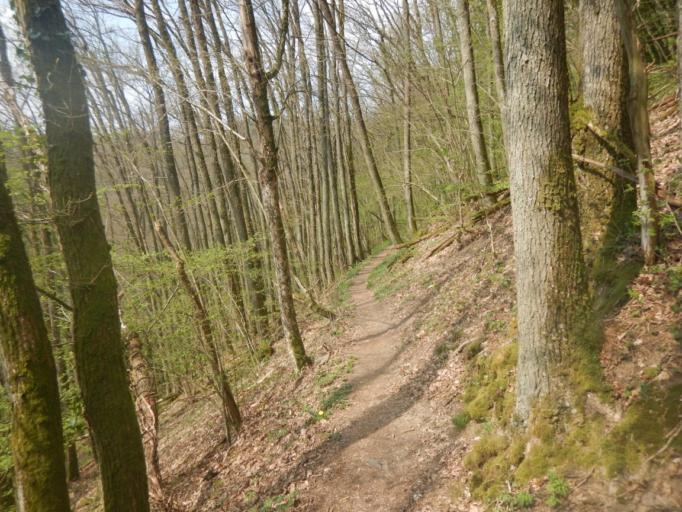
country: LU
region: Diekirch
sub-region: Canton de Wiltz
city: Esch-sur-Sure
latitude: 49.9133
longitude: 5.9219
